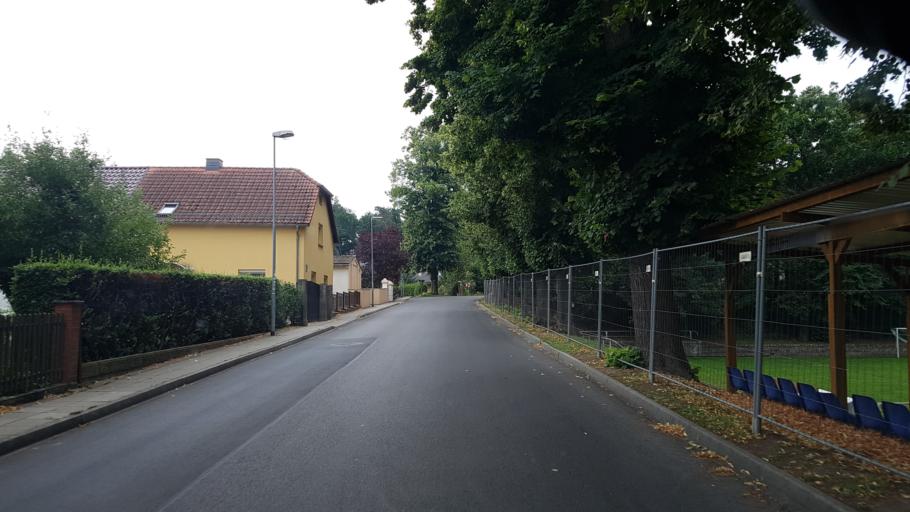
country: DE
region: Brandenburg
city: Hirschfeld
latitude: 51.3820
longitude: 13.6143
